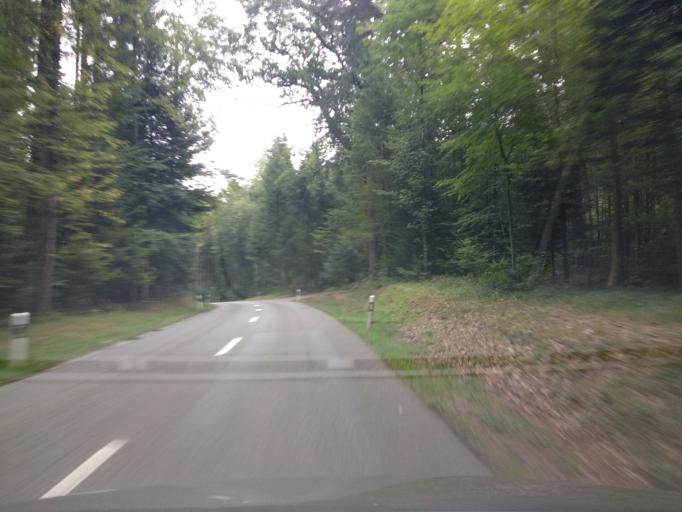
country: CH
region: Thurgau
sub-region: Frauenfeld District
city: Diessenhofen
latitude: 47.6720
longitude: 8.7165
